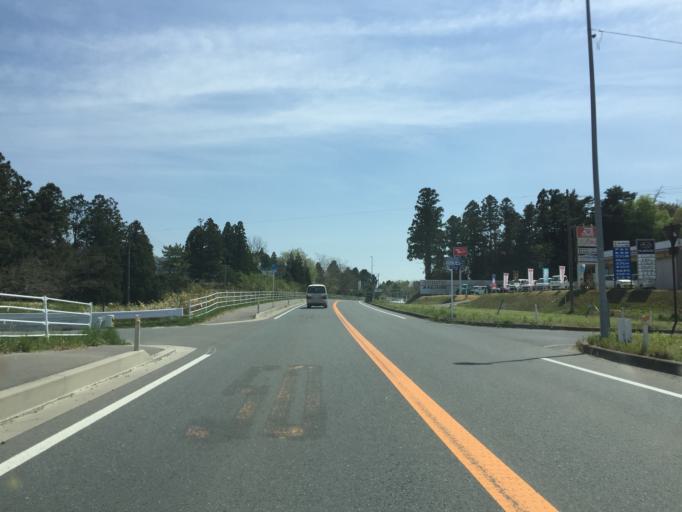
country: JP
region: Miyagi
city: Marumori
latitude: 37.8662
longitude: 140.9201
